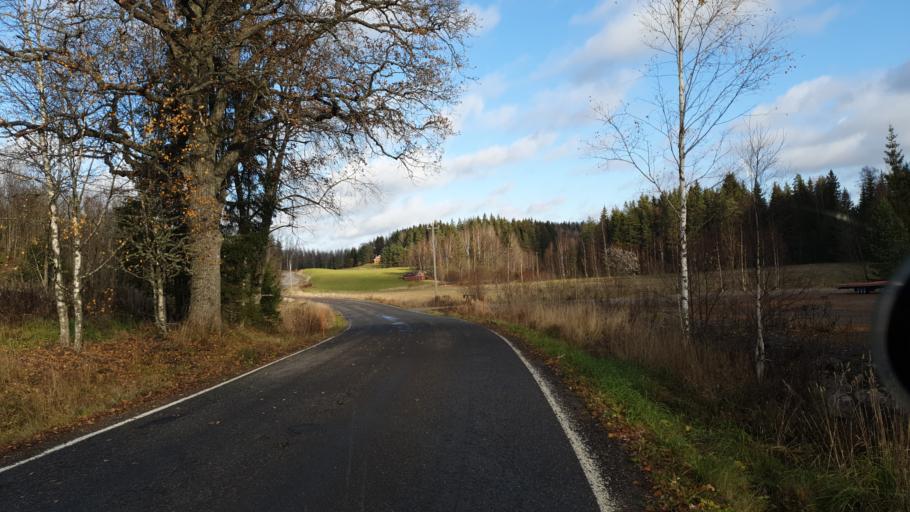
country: FI
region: Uusimaa
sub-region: Helsinki
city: Siuntio
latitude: 60.2658
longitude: 24.3043
